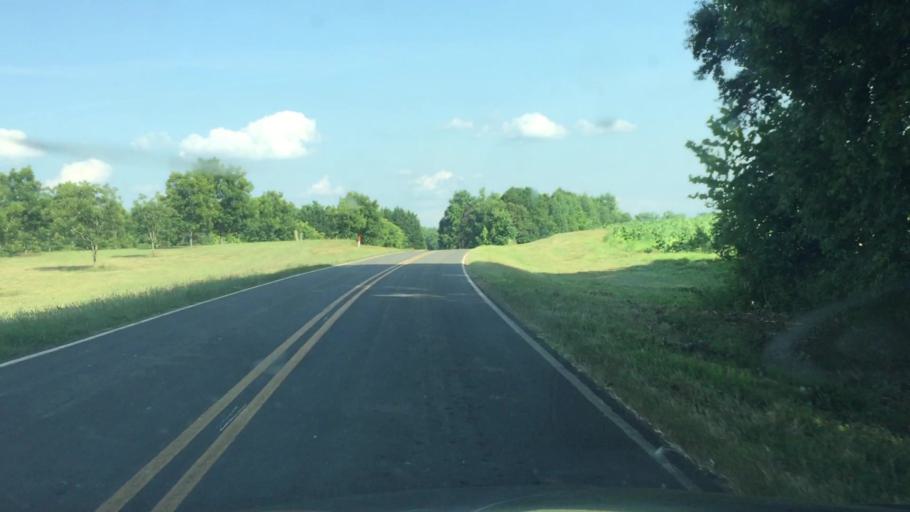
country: US
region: North Carolina
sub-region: Rockingham County
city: Reidsville
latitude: 36.2769
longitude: -79.5882
